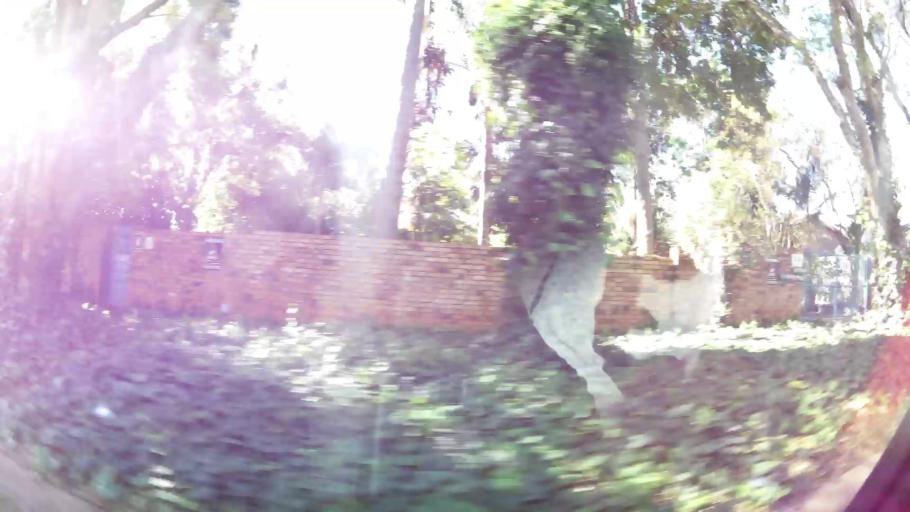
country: ZA
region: Gauteng
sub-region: City of Johannesburg Metropolitan Municipality
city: Roodepoort
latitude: -26.1195
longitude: 27.9192
